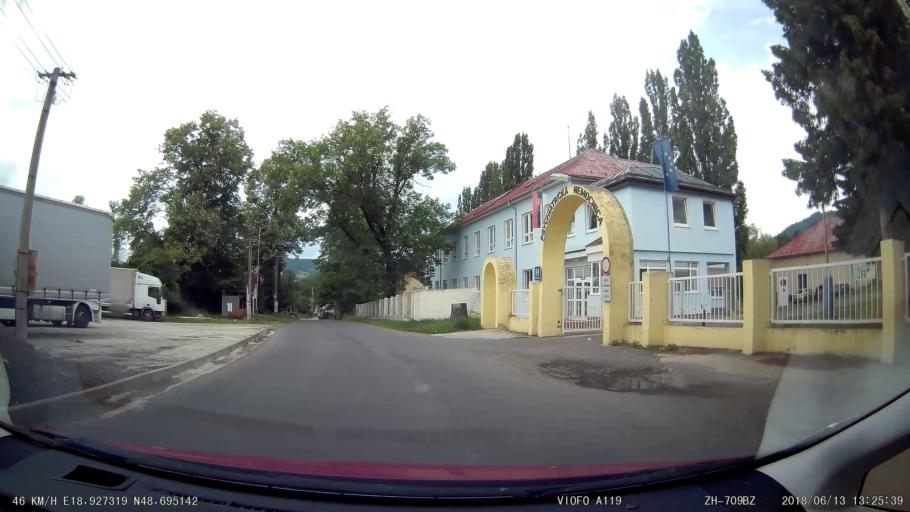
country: SK
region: Banskobystricky
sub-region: Okres Ziar nad Hronom
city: Kremnica
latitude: 48.6952
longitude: 18.9272
